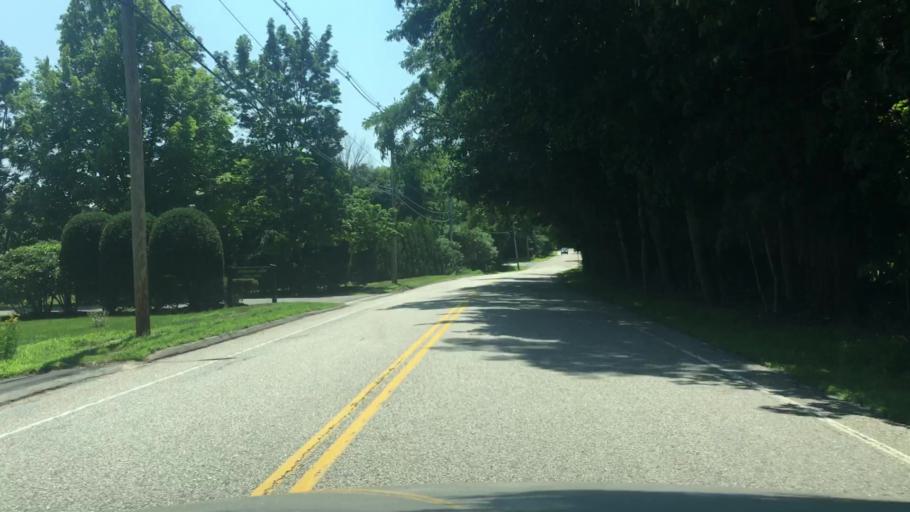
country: US
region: Maine
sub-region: Cumberland County
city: Cumberland Center
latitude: 43.7677
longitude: -70.2715
